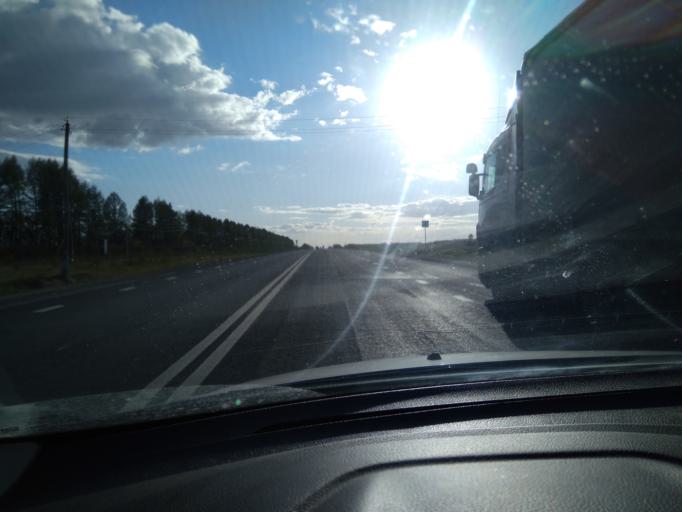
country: RU
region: Sverdlovsk
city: Troitskiy
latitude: 57.0867
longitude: 63.7305
